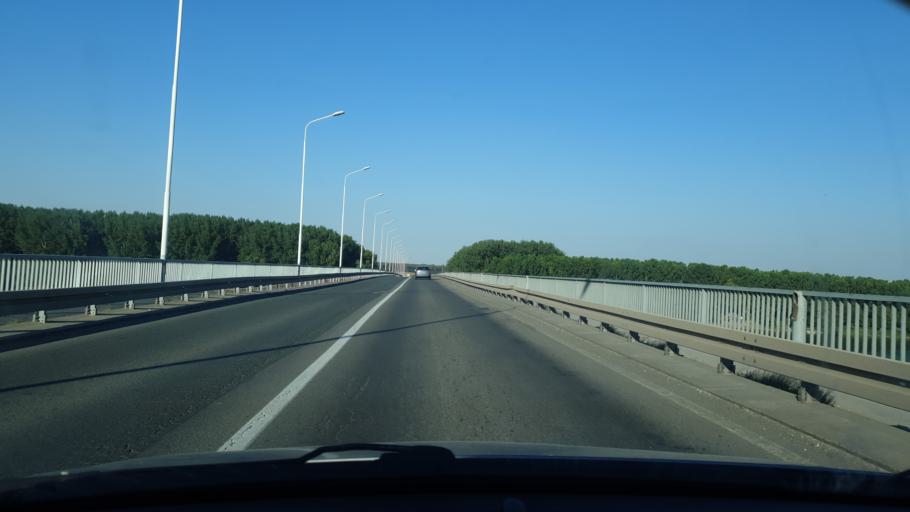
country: RS
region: Central Serbia
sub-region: Macvanski Okrug
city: Sabac
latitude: 44.7584
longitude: 19.7131
